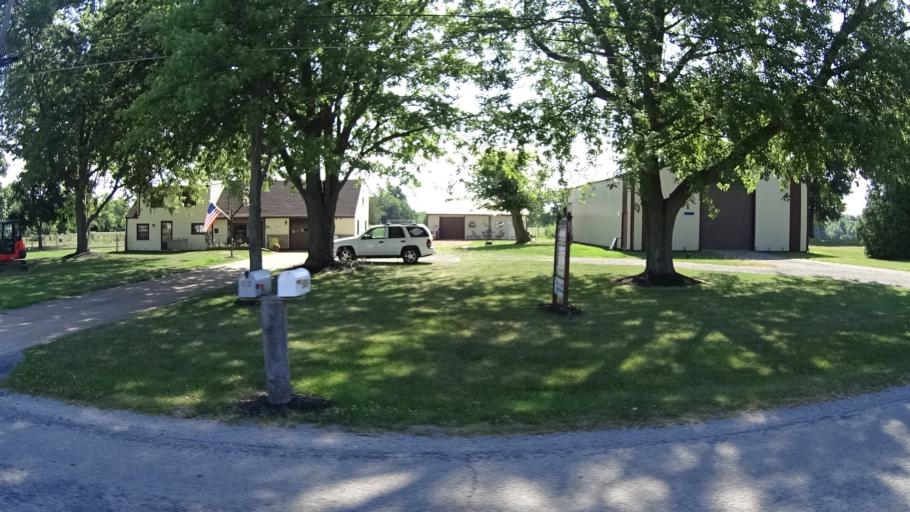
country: US
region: Ohio
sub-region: Huron County
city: Bellevue
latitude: 41.3695
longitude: -82.7949
